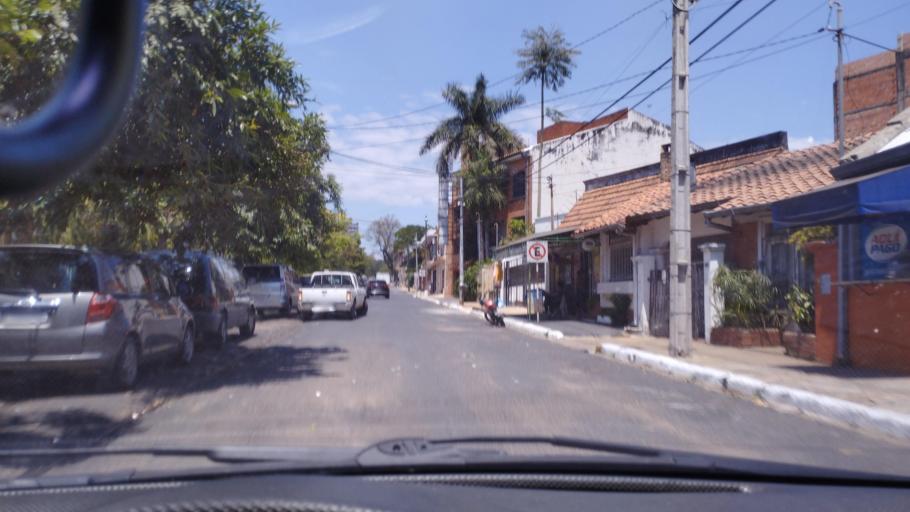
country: PY
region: Asuncion
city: Asuncion
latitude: -25.2809
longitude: -57.6122
